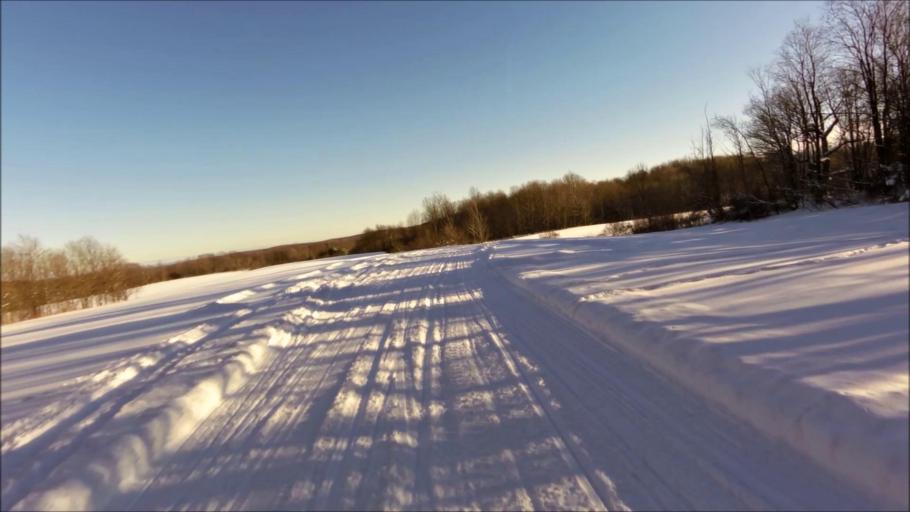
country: US
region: New York
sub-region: Chautauqua County
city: Mayville
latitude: 42.2666
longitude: -79.3799
